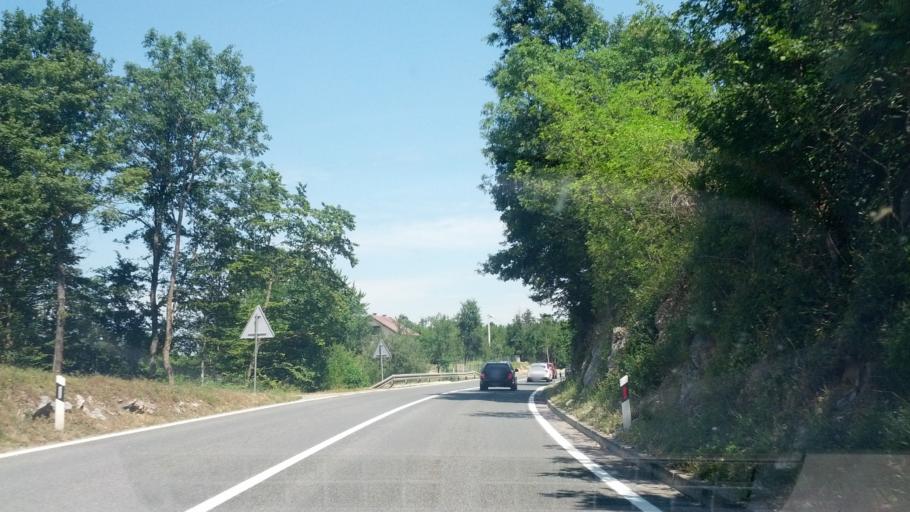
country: HR
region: Karlovacka
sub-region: Grad Karlovac
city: Slunj
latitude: 45.2124
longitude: 15.5441
